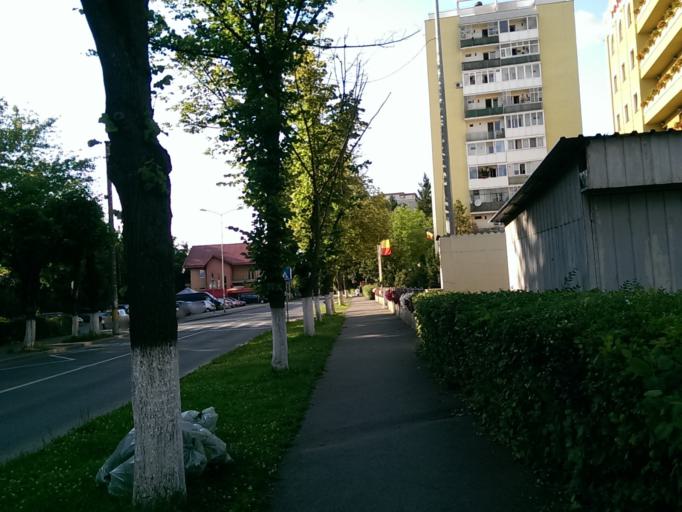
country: RO
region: Cluj
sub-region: Municipiul Cluj-Napoca
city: Cluj-Napoca
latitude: 46.7637
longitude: 23.6208
